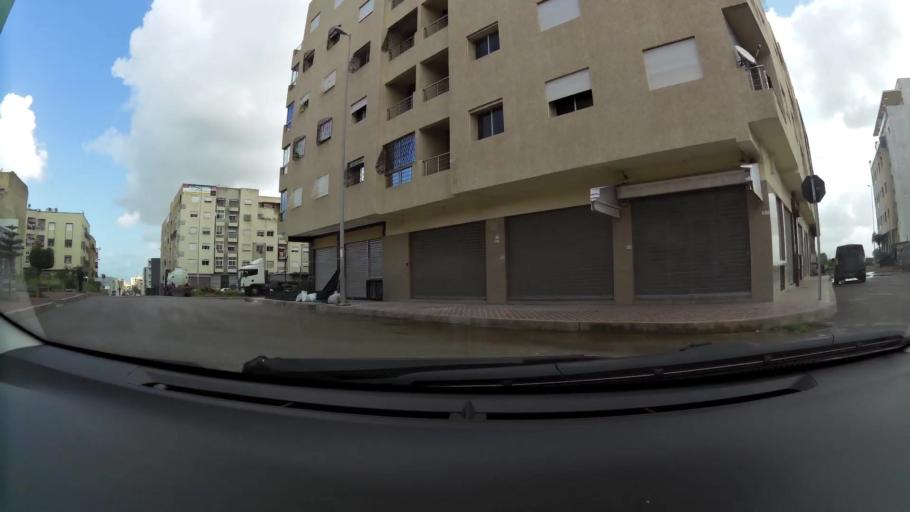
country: MA
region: Grand Casablanca
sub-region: Mediouna
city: Tit Mellil
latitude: 33.5453
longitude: -7.4820
